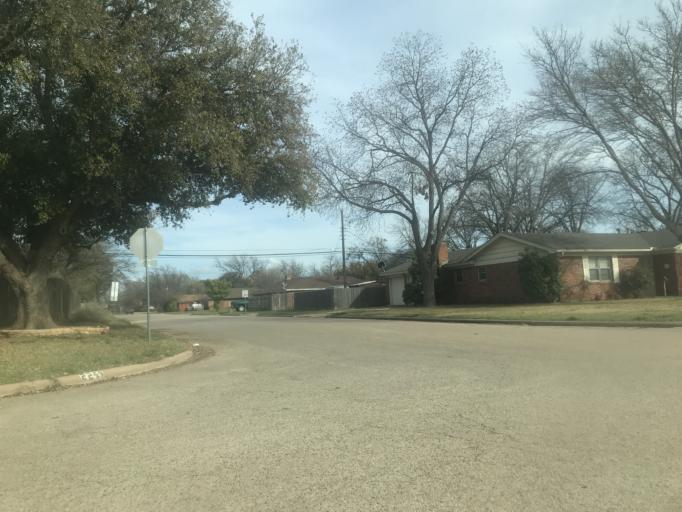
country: US
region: Texas
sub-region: Taylor County
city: Abilene
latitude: 32.4215
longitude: -99.7719
